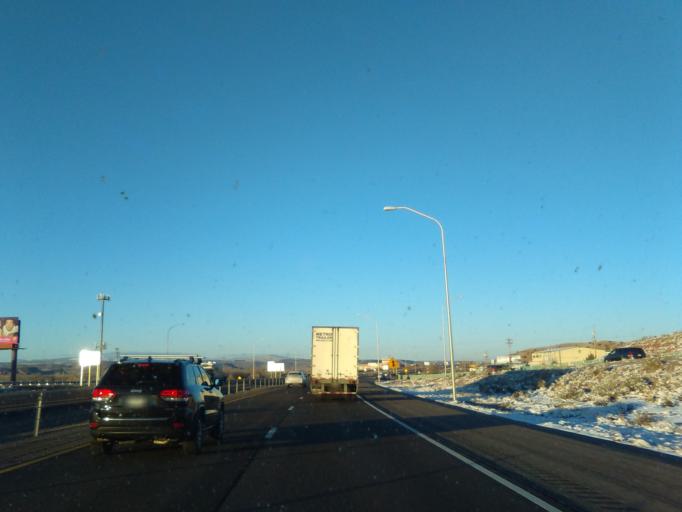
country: US
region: New Mexico
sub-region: Sandoval County
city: Bernalillo
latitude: 35.3178
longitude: -106.5335
